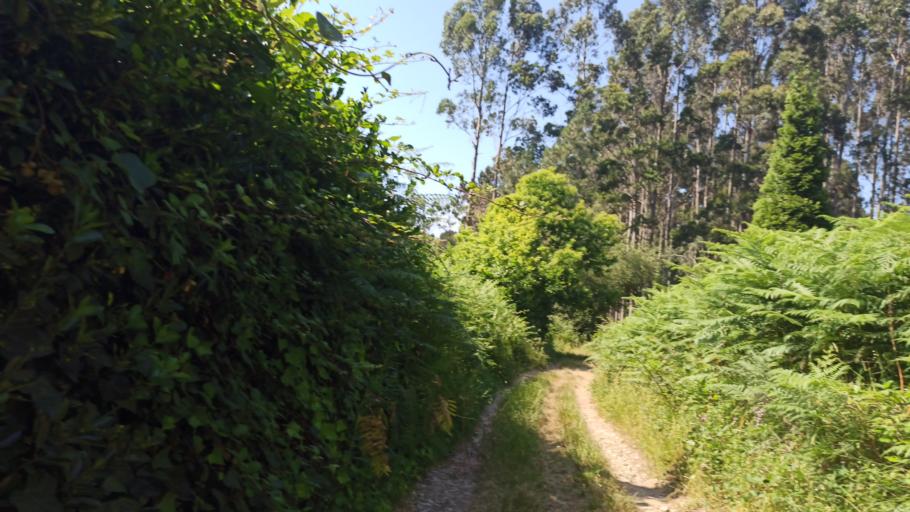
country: ES
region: Galicia
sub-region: Provincia da Coruna
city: Sada
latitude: 43.3797
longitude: -8.2704
